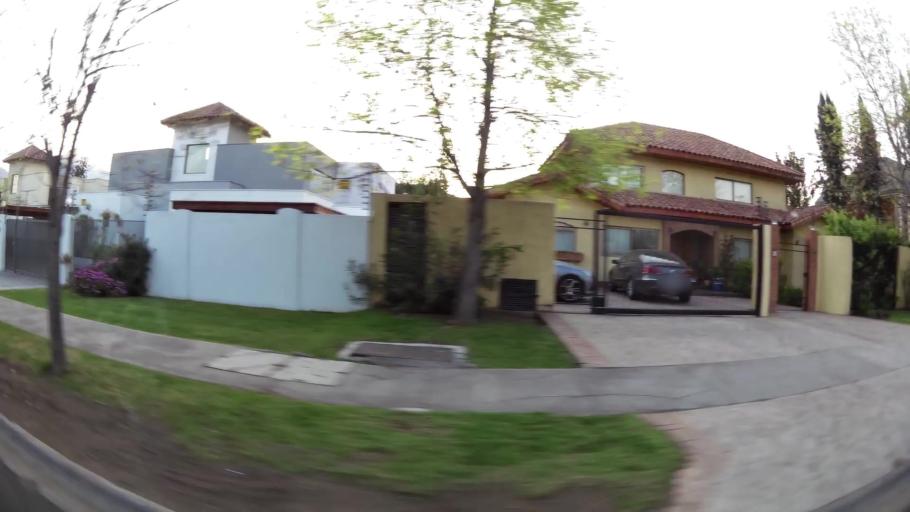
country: CL
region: Santiago Metropolitan
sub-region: Provincia de Chacabuco
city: Chicureo Abajo
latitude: -33.3326
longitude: -70.5429
